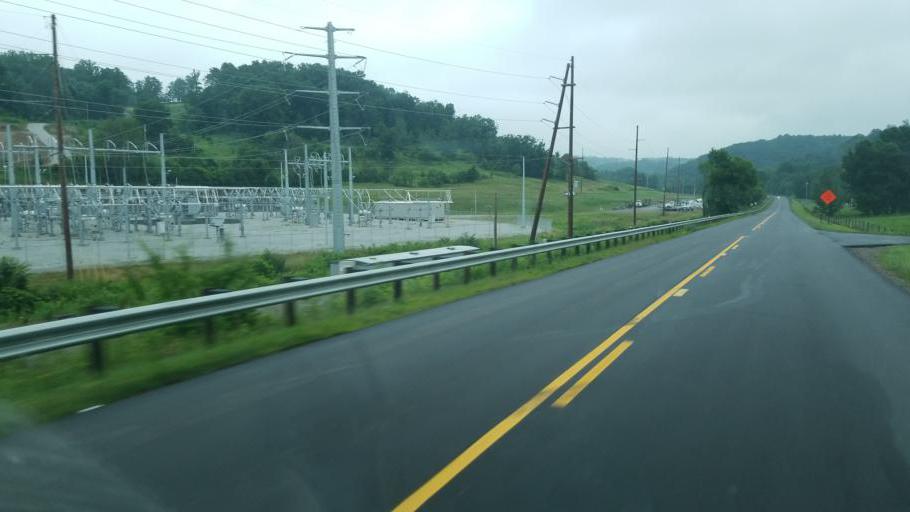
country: US
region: Ohio
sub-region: Tuscarawas County
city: Dennison
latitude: 40.4028
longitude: -81.2420
